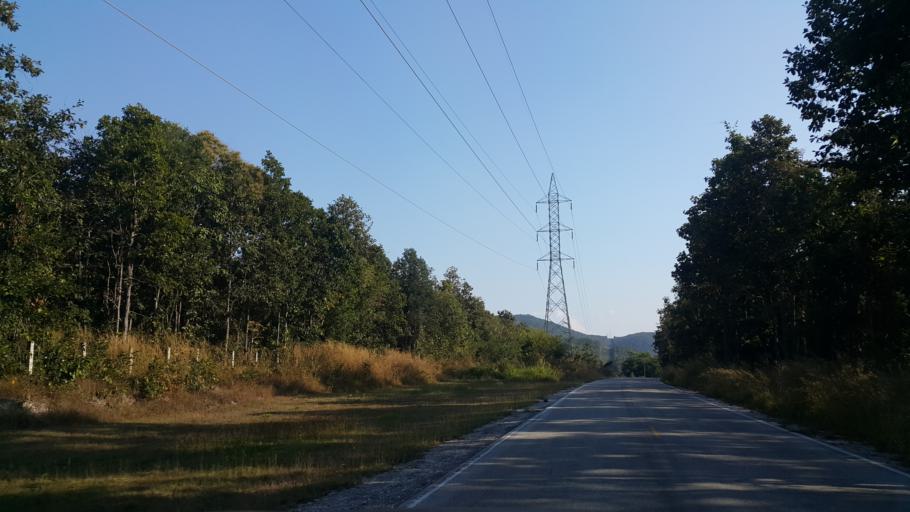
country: TH
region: Lamphun
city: Mae Tha
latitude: 18.5192
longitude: 99.1112
